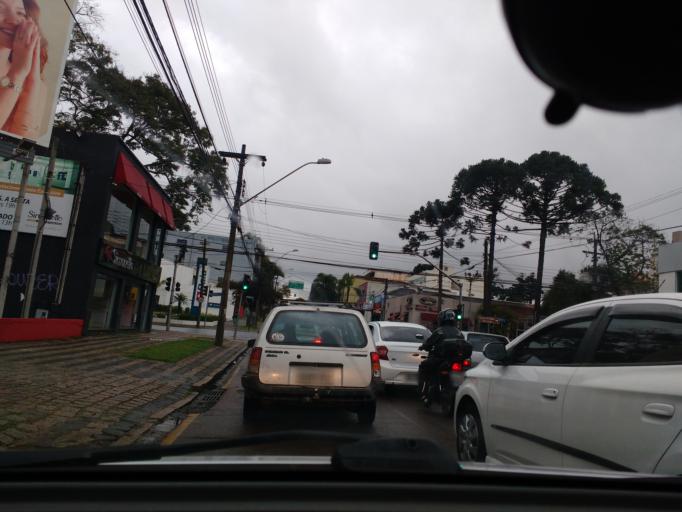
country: BR
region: Parana
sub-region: Curitiba
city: Curitiba
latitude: -25.4260
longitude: -49.2854
